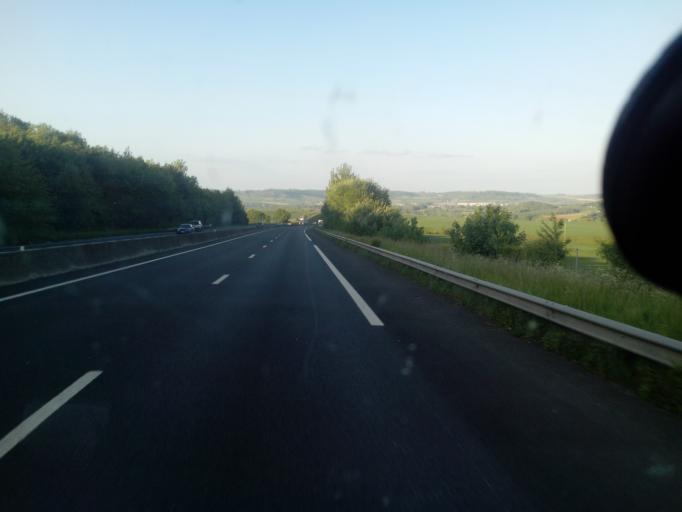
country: FR
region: Haute-Normandie
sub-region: Departement de la Seine-Maritime
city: Mesnieres-en-Bray
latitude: 49.7082
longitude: 1.3781
